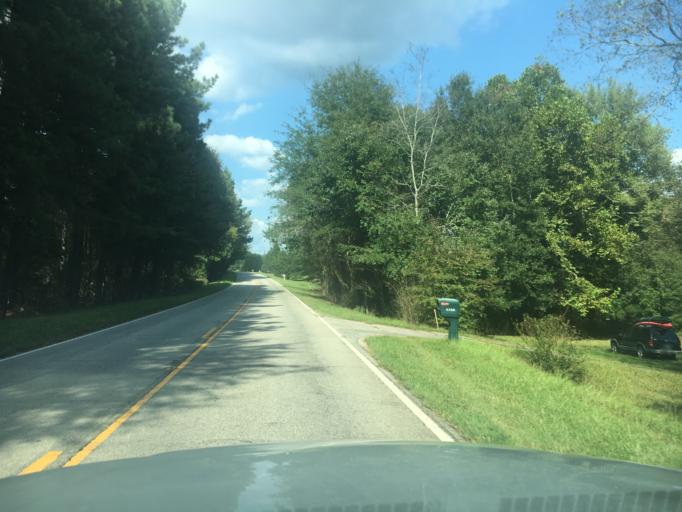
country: US
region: South Carolina
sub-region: Anderson County
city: Pendleton
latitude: 34.6790
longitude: -82.7536
